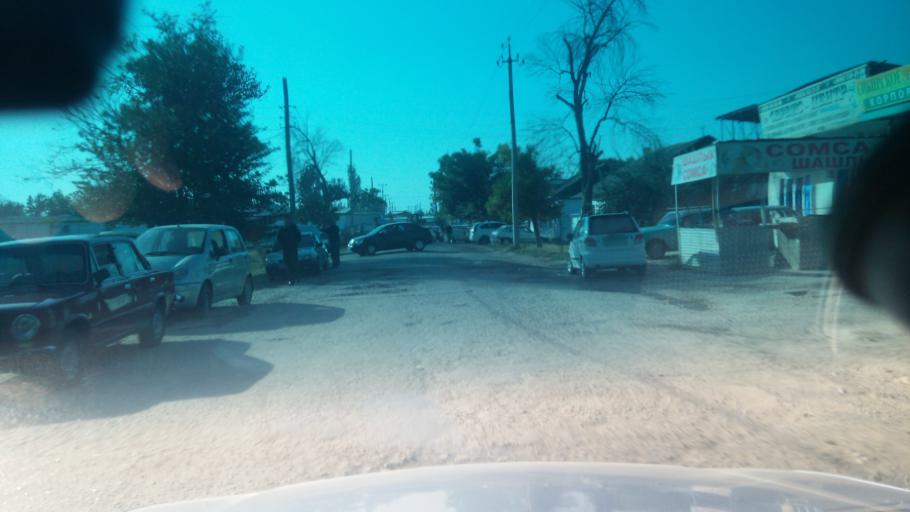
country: UZ
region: Sirdaryo
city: Guliston
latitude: 40.4959
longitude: 68.7693
